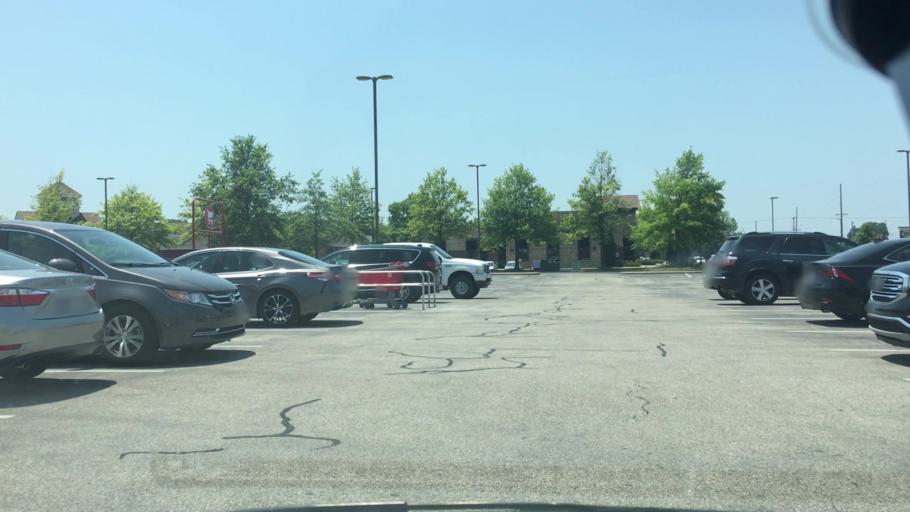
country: US
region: Indiana
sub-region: Vanderburgh County
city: Melody Hill
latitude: 37.9758
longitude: -87.4712
